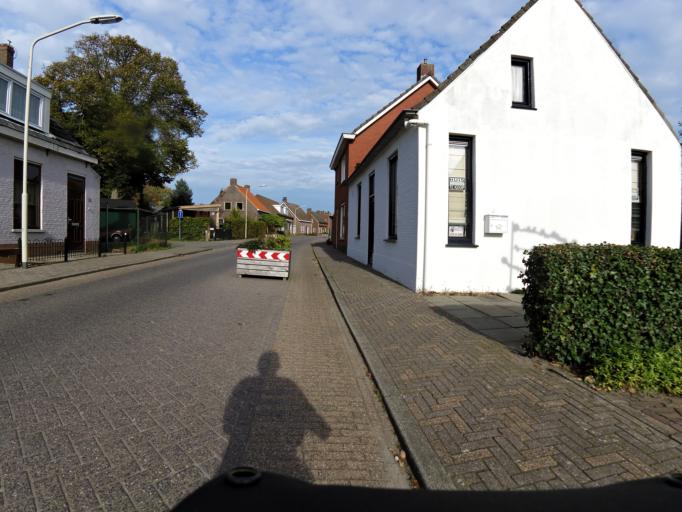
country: NL
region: North Brabant
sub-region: Gemeente Woensdrecht
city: Woensdrecht
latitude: 51.3973
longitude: 4.3287
